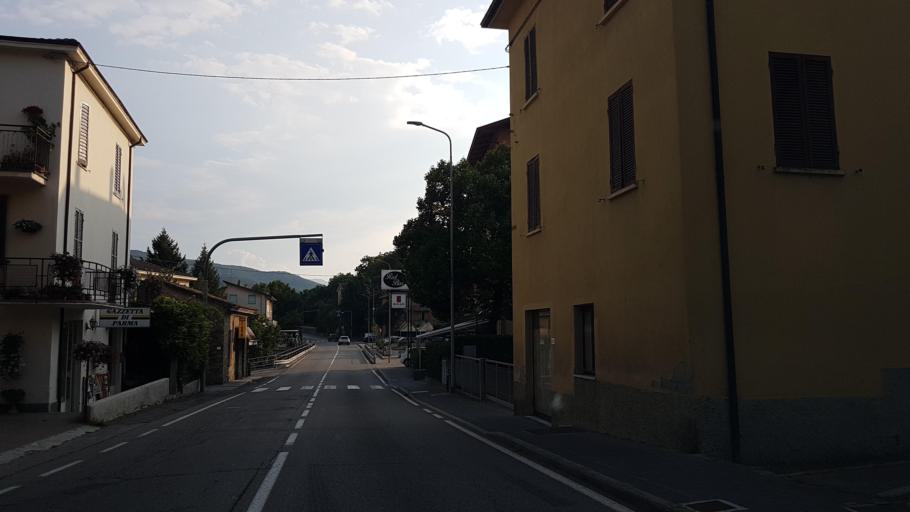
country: IT
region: Emilia-Romagna
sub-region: Provincia di Parma
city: Solignano
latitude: 44.6141
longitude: 9.9781
